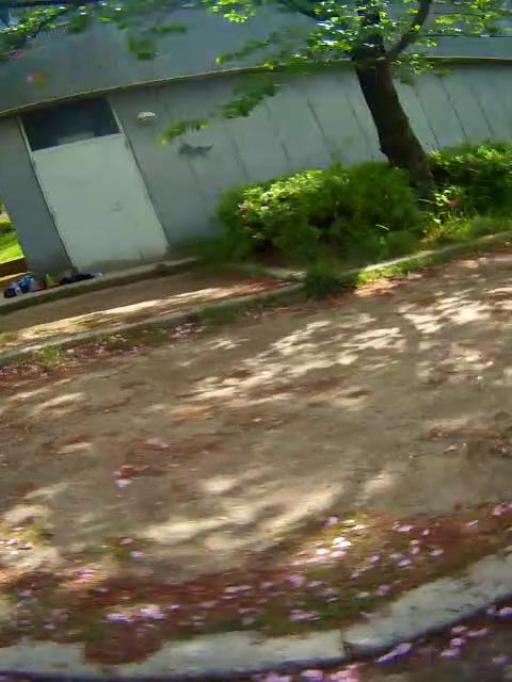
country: JP
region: Osaka
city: Osaka-shi
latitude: 34.7041
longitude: 135.5198
